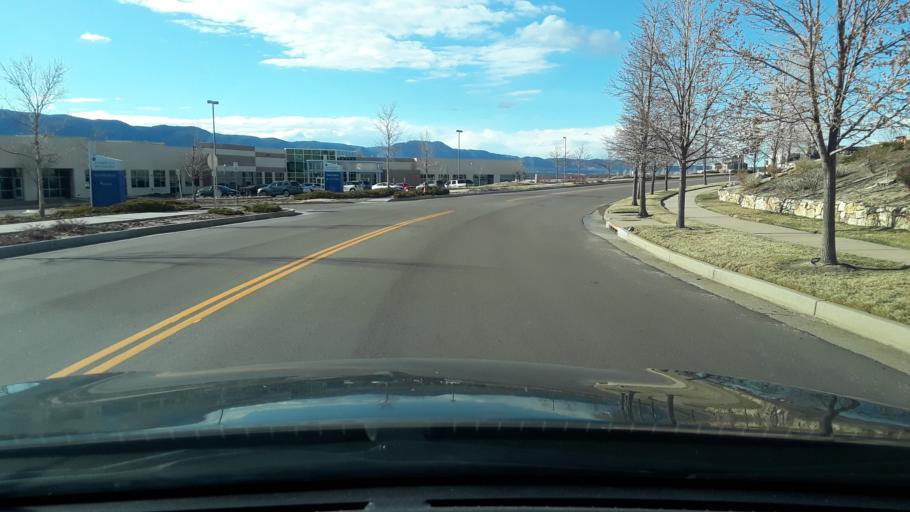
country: US
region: Colorado
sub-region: El Paso County
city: Air Force Academy
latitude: 38.9827
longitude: -104.8047
